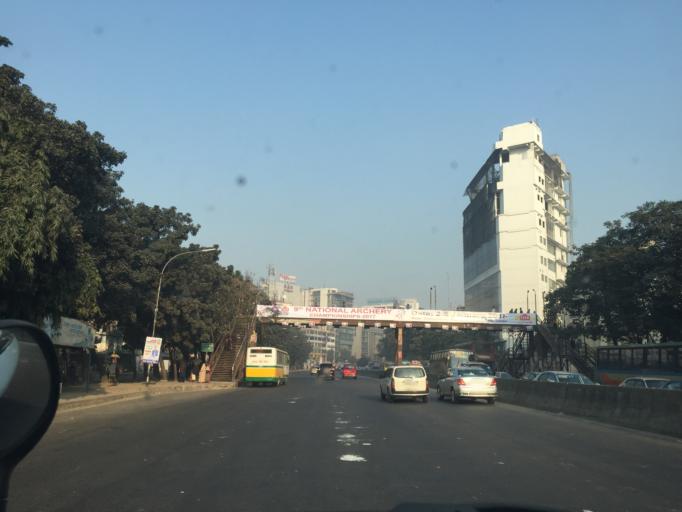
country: BD
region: Dhaka
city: Tungi
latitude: 23.8585
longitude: 90.4018
